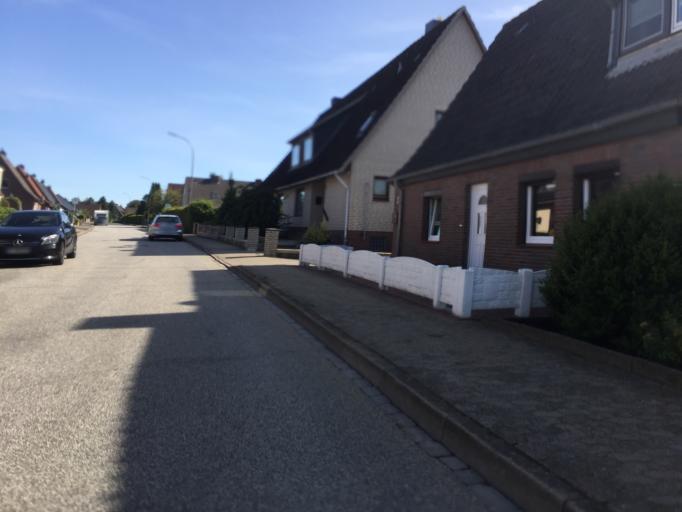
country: DE
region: Schleswig-Holstein
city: Kremperheide
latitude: 53.9065
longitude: 9.4926
